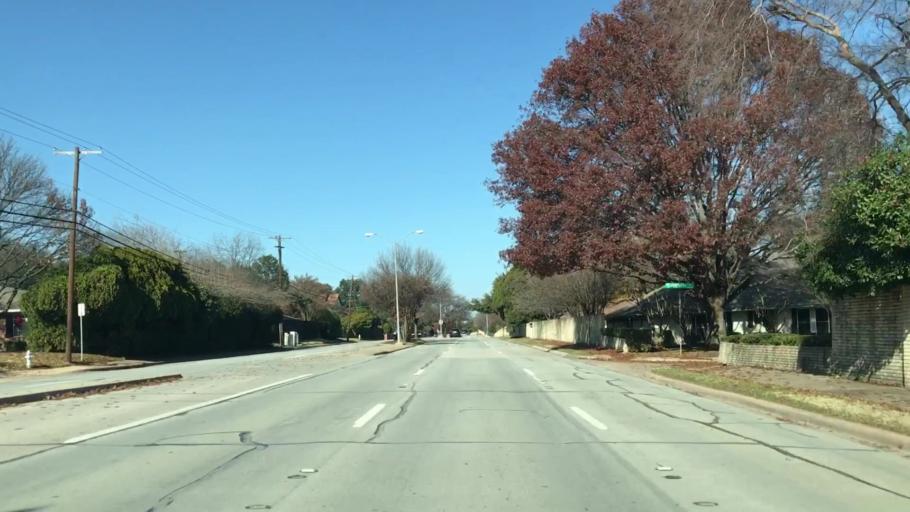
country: US
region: Texas
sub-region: Dallas County
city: University Park
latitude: 32.8870
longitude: -96.7867
